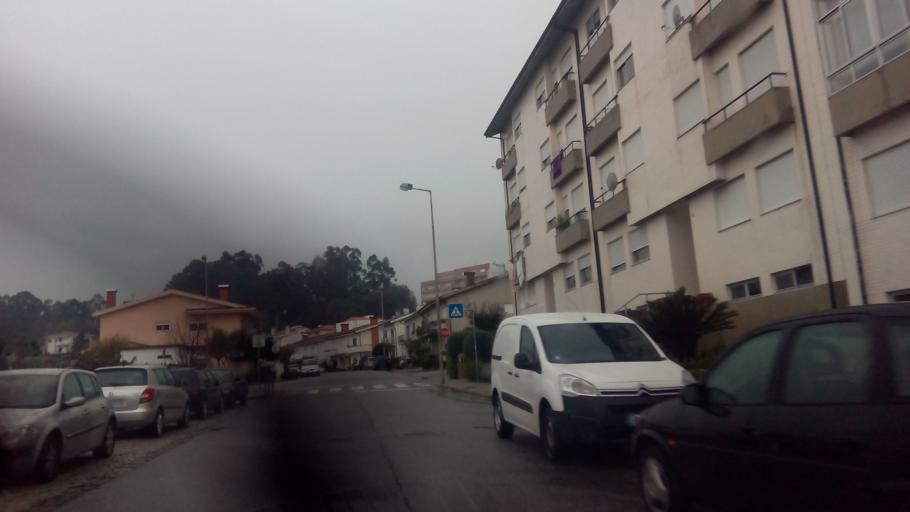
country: PT
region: Porto
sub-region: Paredes
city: Casteloes de Cepeda
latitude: 41.2073
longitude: -8.3388
